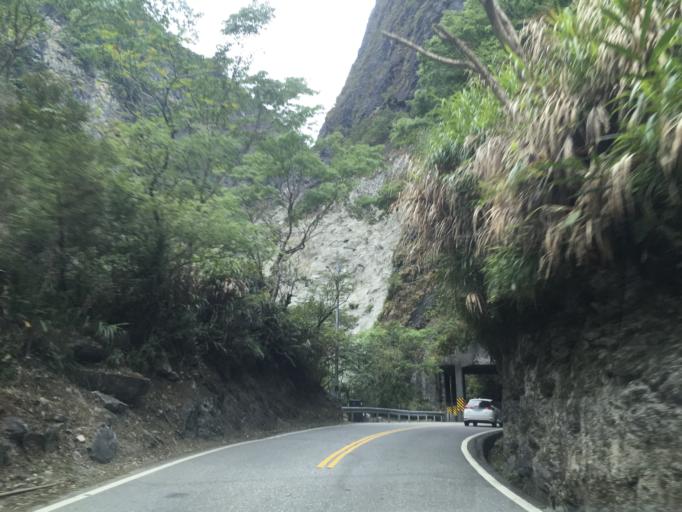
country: TW
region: Taiwan
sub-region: Hualien
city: Hualian
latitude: 24.1738
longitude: 121.5245
